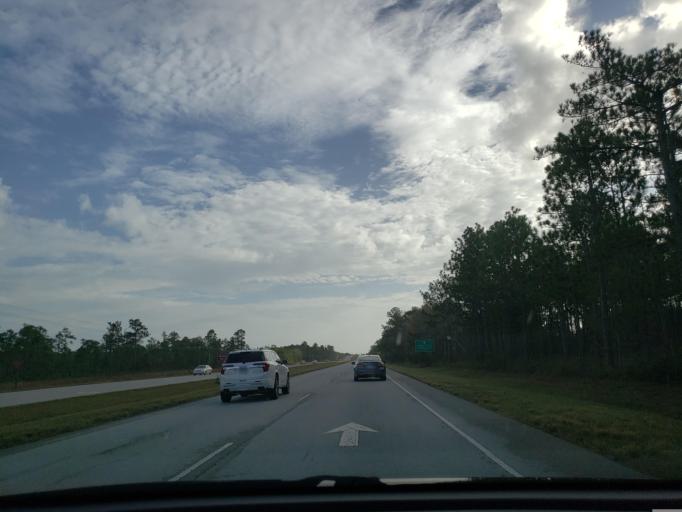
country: US
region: North Carolina
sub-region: Onslow County
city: Sneads Ferry
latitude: 34.6047
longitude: -77.4825
